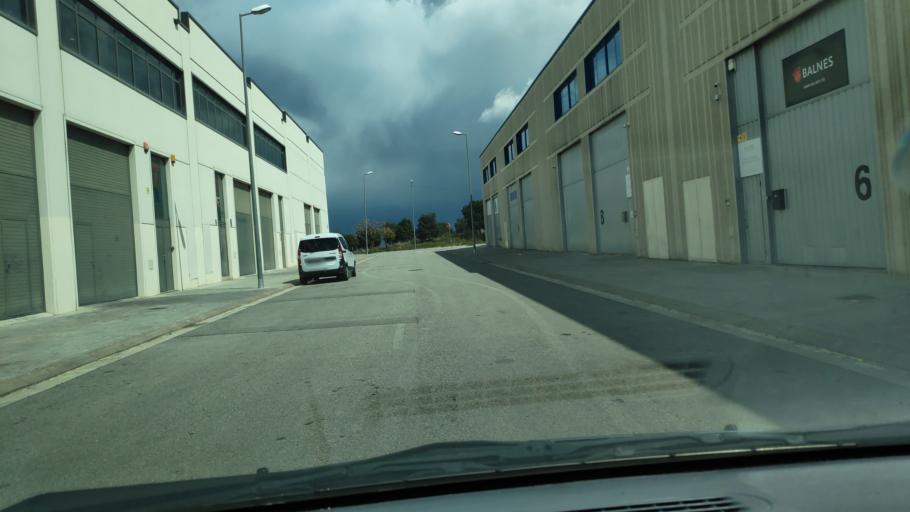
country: ES
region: Catalonia
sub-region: Provincia de Barcelona
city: Polinya
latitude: 41.5421
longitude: 2.1359
